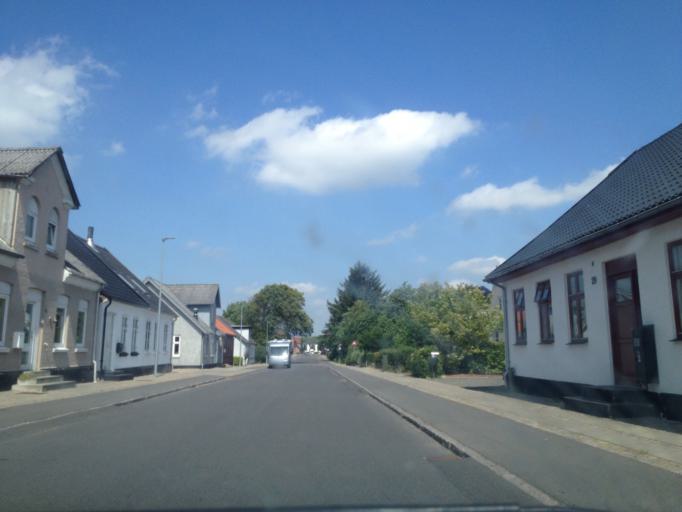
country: DK
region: South Denmark
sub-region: Kolding Kommune
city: Vamdrup
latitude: 55.4232
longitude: 9.2784
